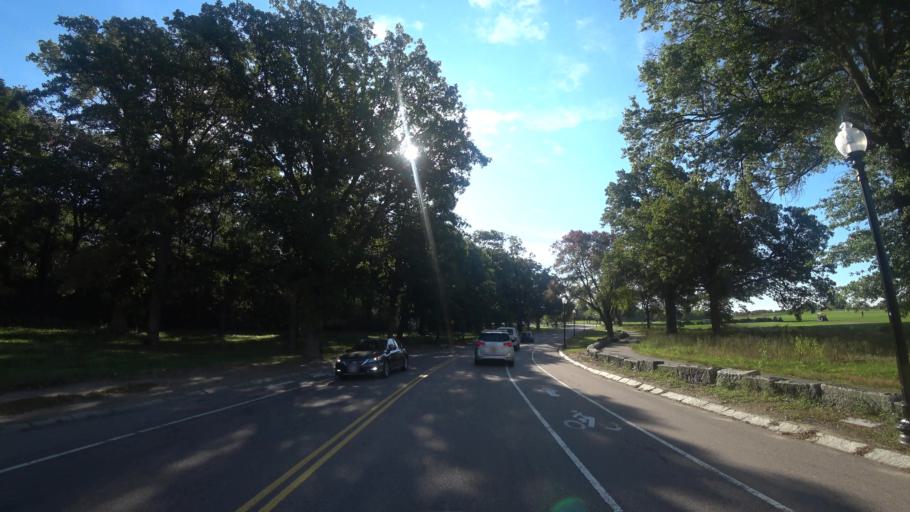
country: US
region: Massachusetts
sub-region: Suffolk County
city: Jamaica Plain
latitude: 42.3047
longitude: -71.0922
